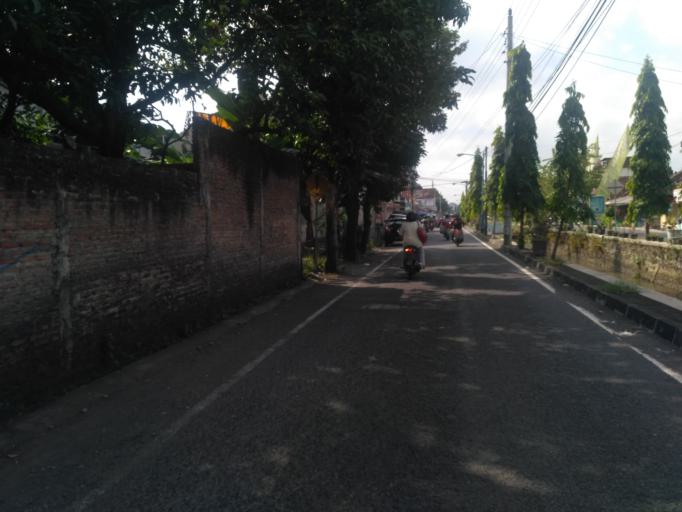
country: ID
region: Daerah Istimewa Yogyakarta
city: Yogyakarta
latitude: -7.7613
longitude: 110.3622
